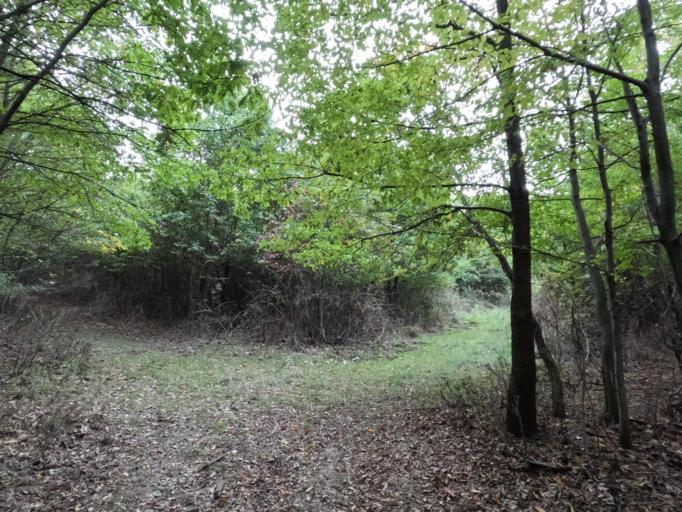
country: HU
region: Tolna
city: Szentgalpuszta
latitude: 46.3176
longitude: 18.6430
